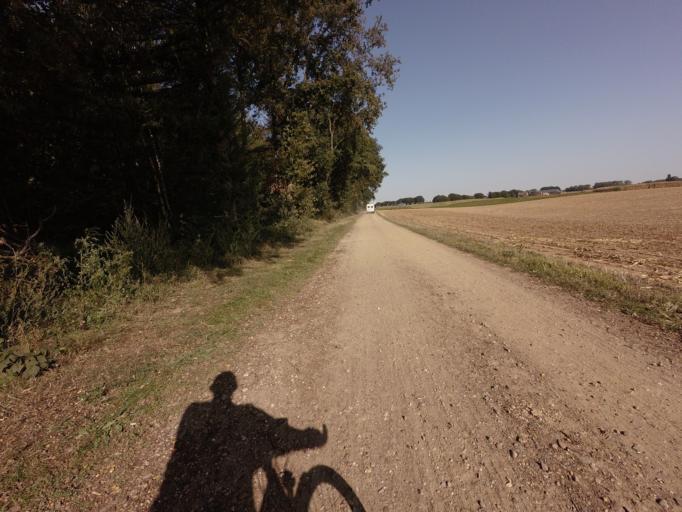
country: NL
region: Limburg
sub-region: Gemeente Roerdalen
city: Sint Odilienberg
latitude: 51.1564
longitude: 5.9806
